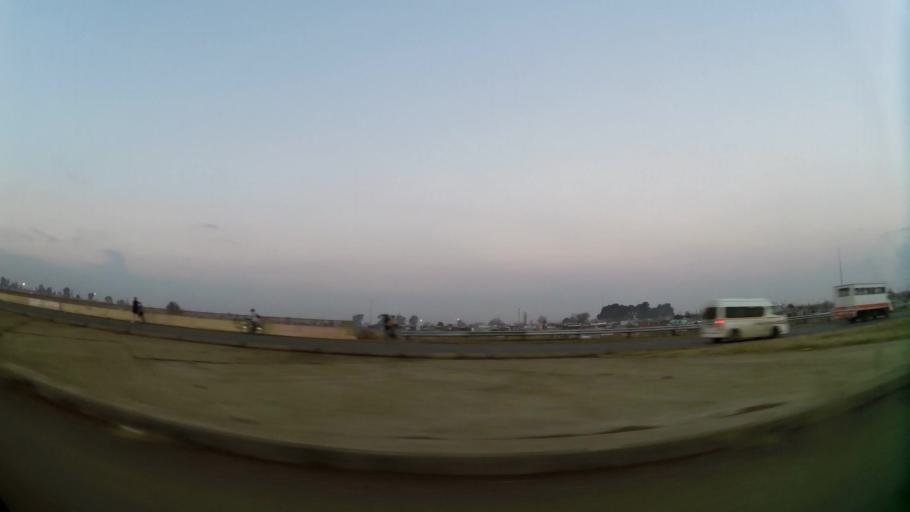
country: ZA
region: Gauteng
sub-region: City of Johannesburg Metropolitan Municipality
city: Orange Farm
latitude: -26.5462
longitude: 27.8301
